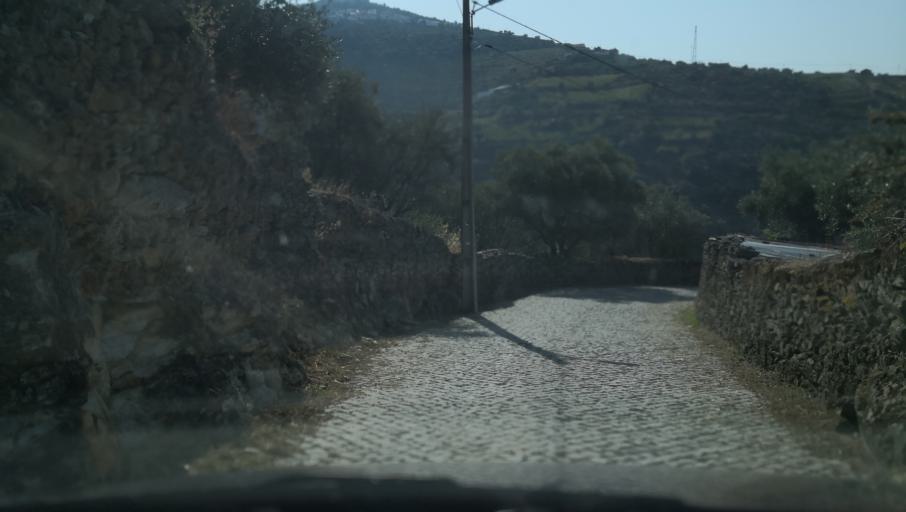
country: PT
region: Vila Real
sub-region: Sabrosa
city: Vilela
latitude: 41.2009
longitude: -7.5462
